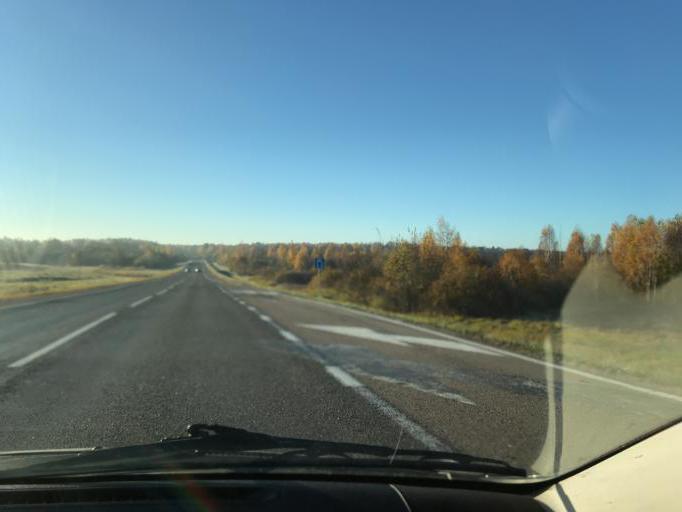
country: BY
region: Vitebsk
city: Vitebsk
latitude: 54.9077
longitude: 30.3761
